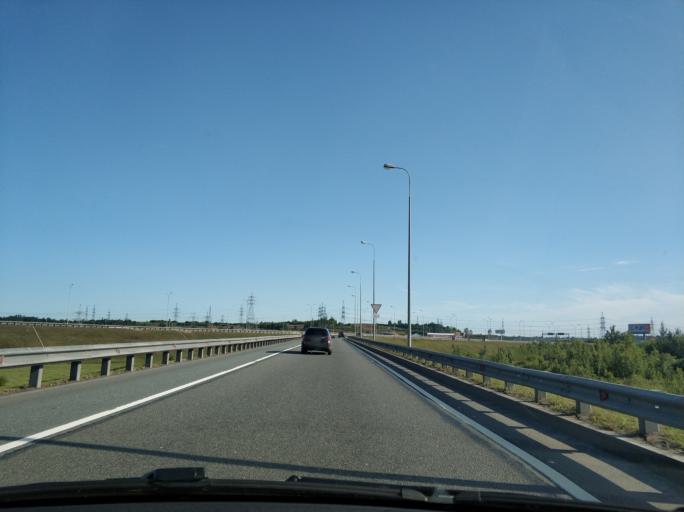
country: RU
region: Leningrad
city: Bugry
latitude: 60.0917
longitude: 30.3724
